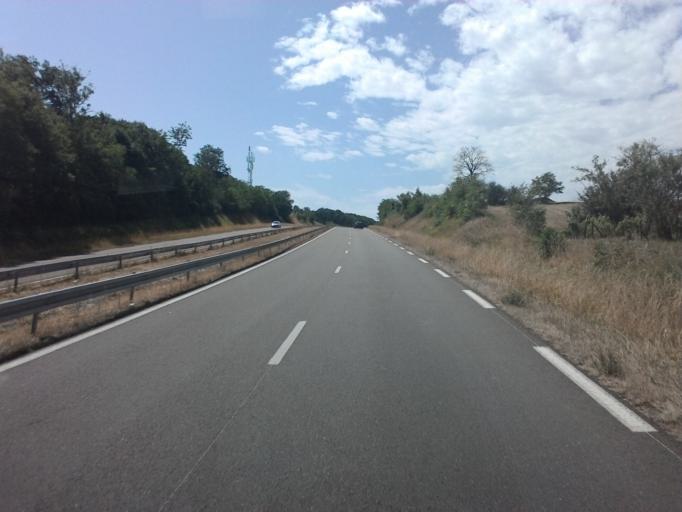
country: FR
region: Franche-Comte
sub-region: Departement du Jura
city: Cousance
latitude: 46.5527
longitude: 5.4040
